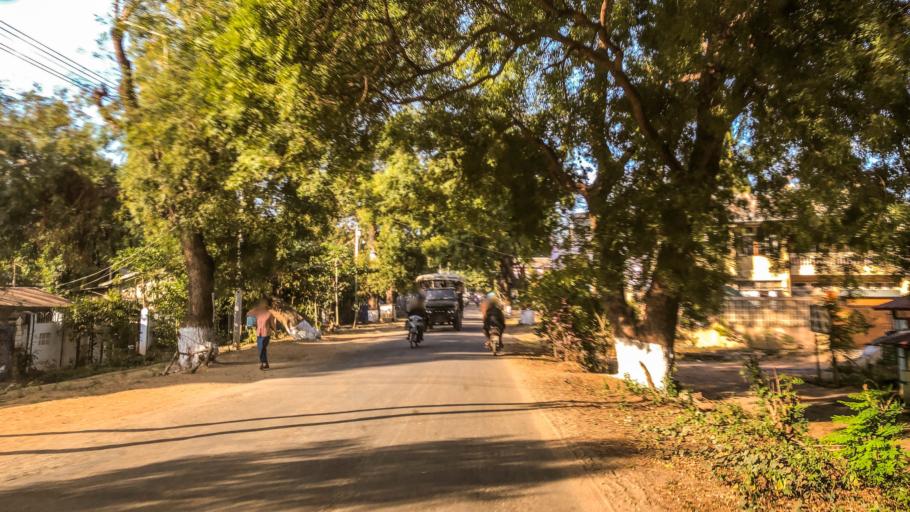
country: MM
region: Magway
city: Magway
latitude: 19.9667
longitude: 95.0398
